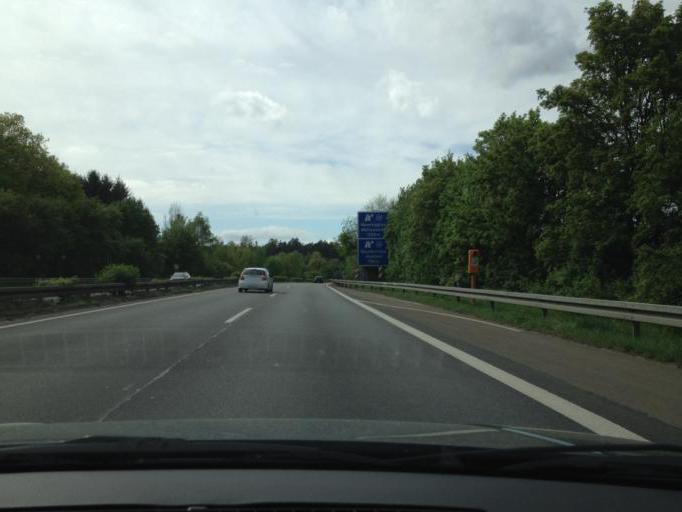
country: DE
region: Saarland
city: Kirkel
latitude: 49.3118
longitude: 7.2479
